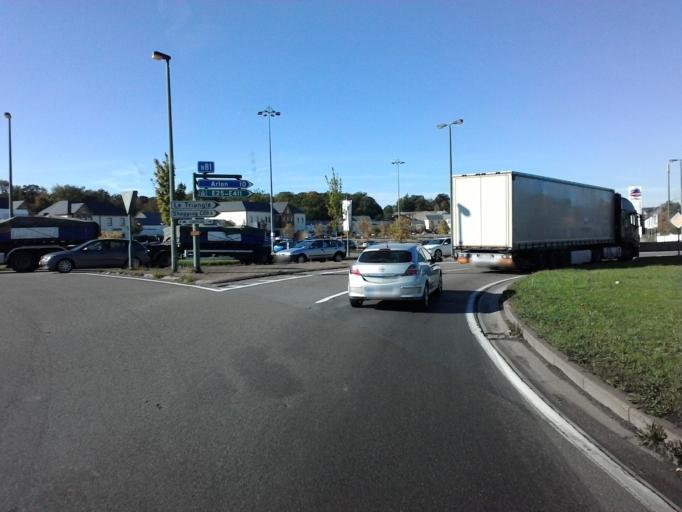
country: BE
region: Wallonia
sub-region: Province du Luxembourg
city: Messancy
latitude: 49.6081
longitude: 5.8106
